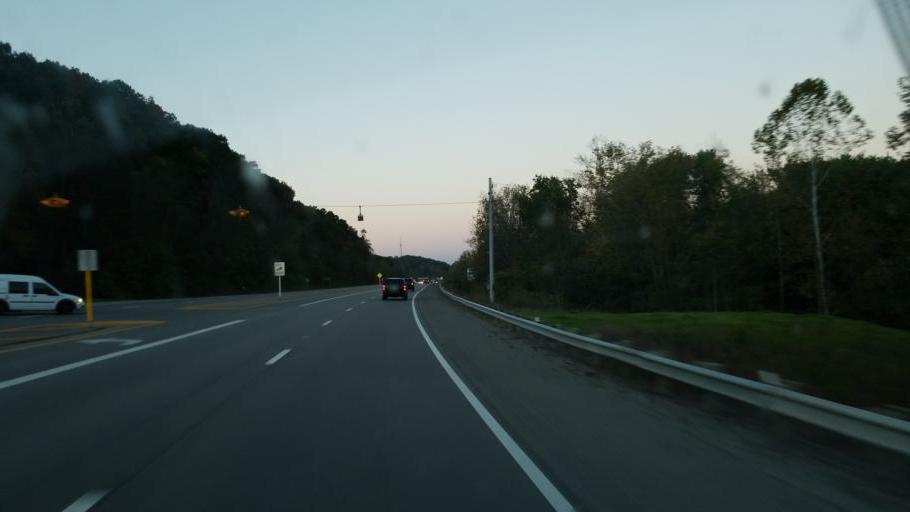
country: US
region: Ohio
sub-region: Ross County
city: Chillicothe
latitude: 39.2473
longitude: -82.9833
